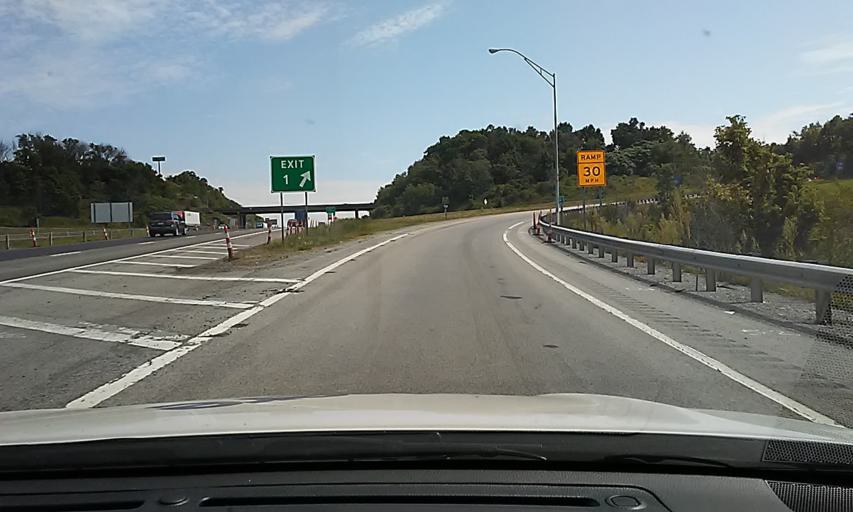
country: US
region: West Virginia
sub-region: Monongalia County
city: Morgantown
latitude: 39.5825
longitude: -79.9578
